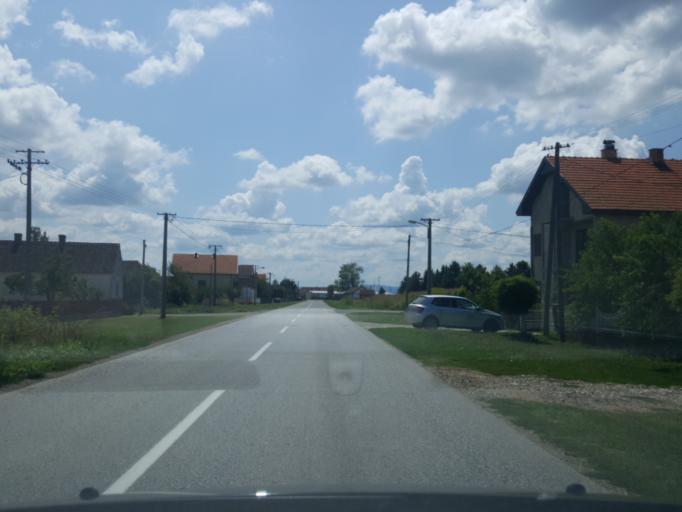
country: RS
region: Central Serbia
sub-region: Macvanski Okrug
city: Bogatic
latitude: 44.8239
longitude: 19.4777
